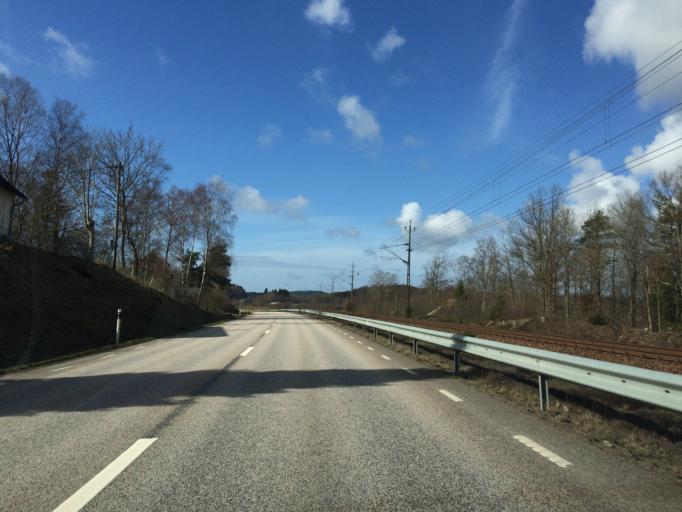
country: SE
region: Halland
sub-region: Laholms Kommun
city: Knared
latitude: 56.5081
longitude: 13.3408
